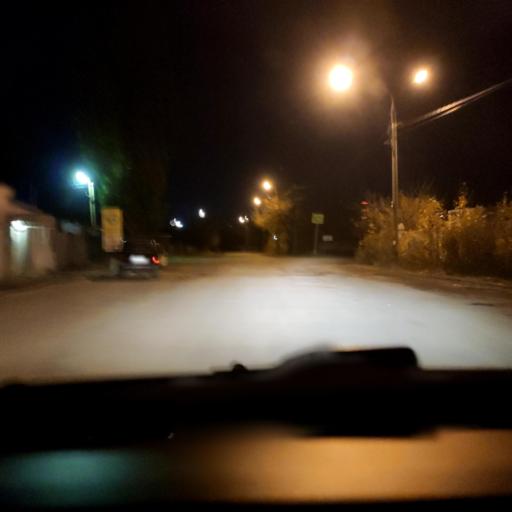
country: RU
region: Voronezj
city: Voronezh
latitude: 51.6763
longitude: 39.1743
